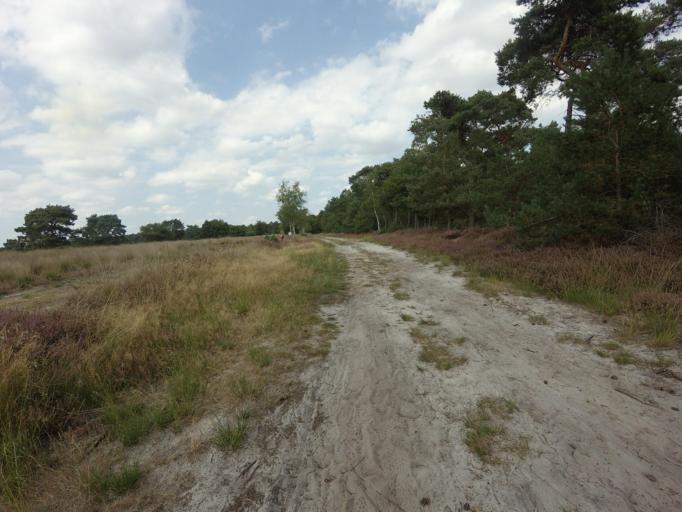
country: NL
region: North Brabant
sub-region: Gemeente Someren
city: Someren
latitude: 51.4010
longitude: 5.6624
